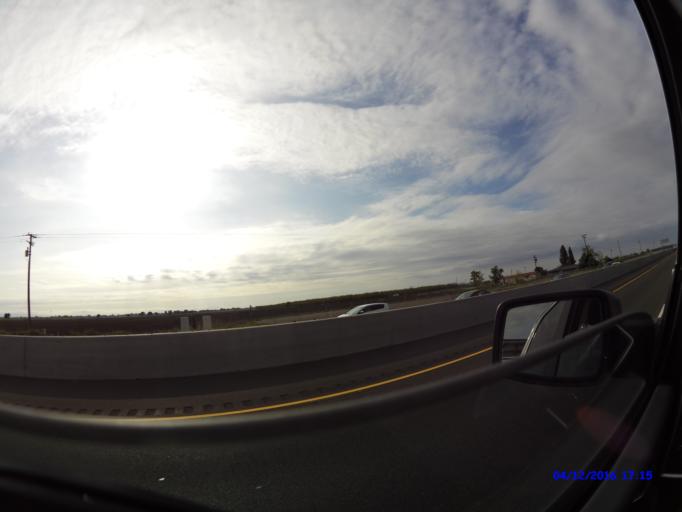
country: US
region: California
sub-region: San Joaquin County
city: French Camp
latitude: 37.8777
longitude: -121.2197
